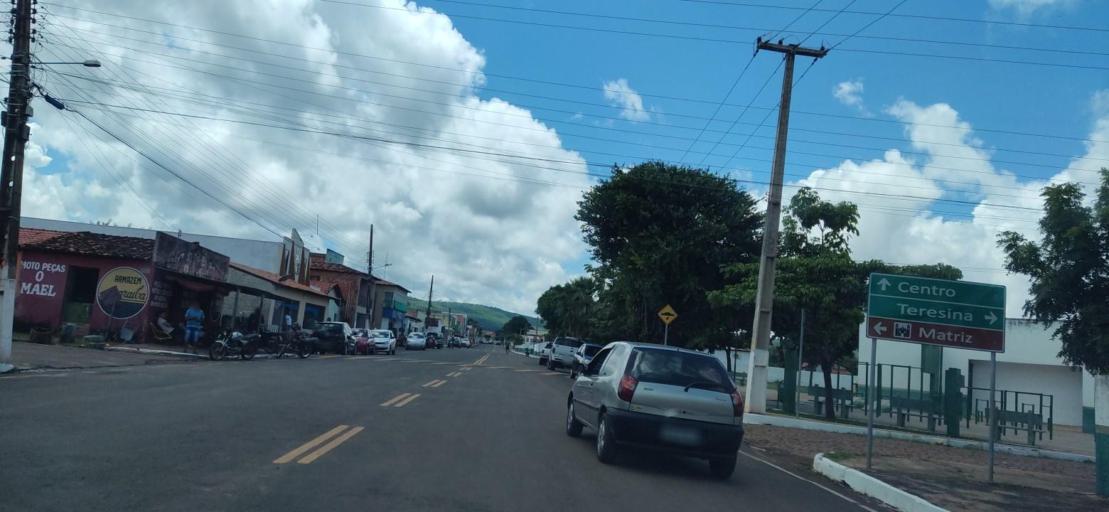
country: BR
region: Piaui
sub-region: Valenca Do Piaui
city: Valenca do Piaui
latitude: -6.1111
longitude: -41.7920
